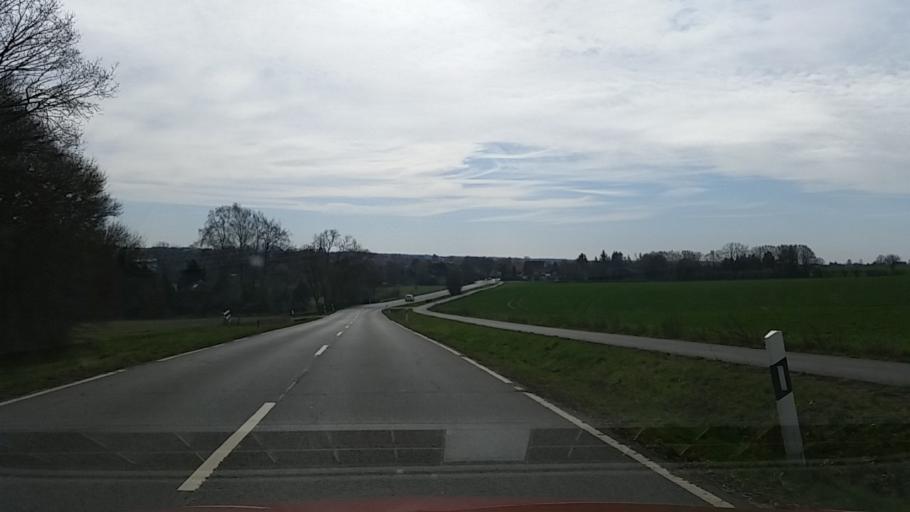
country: DE
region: Lower Saxony
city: Weyhausen
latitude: 52.4061
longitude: 10.6927
